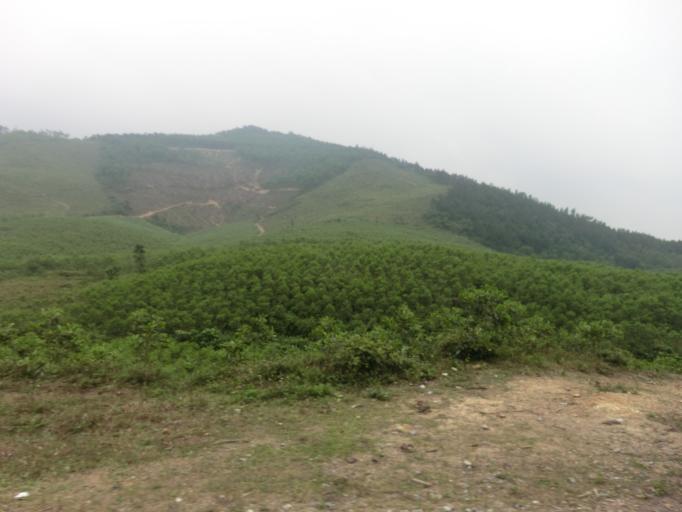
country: VN
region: Quang Binh
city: Ba Don
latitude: 17.6764
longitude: 106.4240
